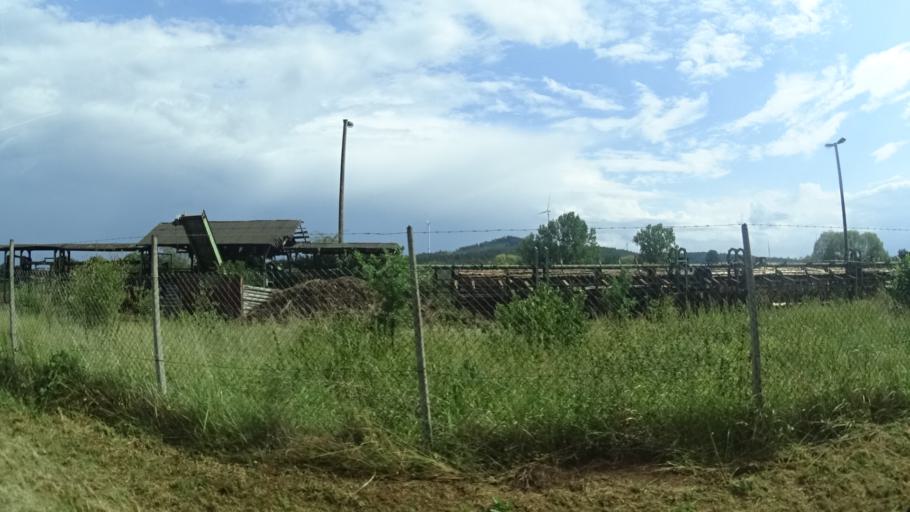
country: DE
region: Hesse
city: Grebenau
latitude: 50.7698
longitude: 9.5193
